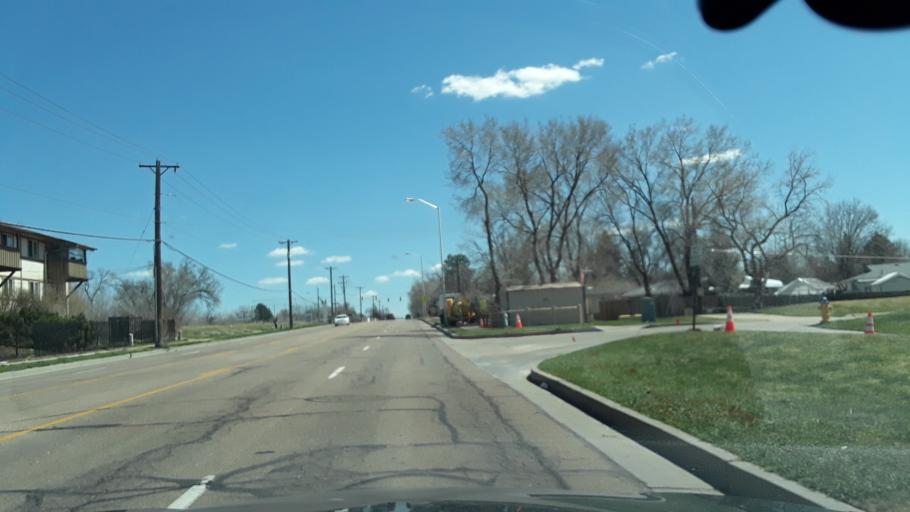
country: US
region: Colorado
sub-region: El Paso County
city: Cimarron Hills
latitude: 38.8470
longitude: -104.7550
